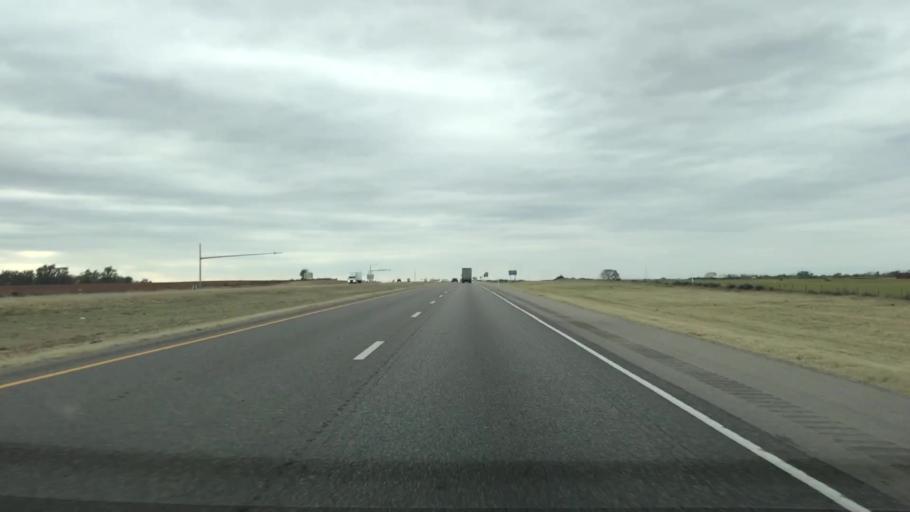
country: US
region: Oklahoma
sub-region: Beckham County
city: Erick
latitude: 35.2295
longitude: -99.9793
